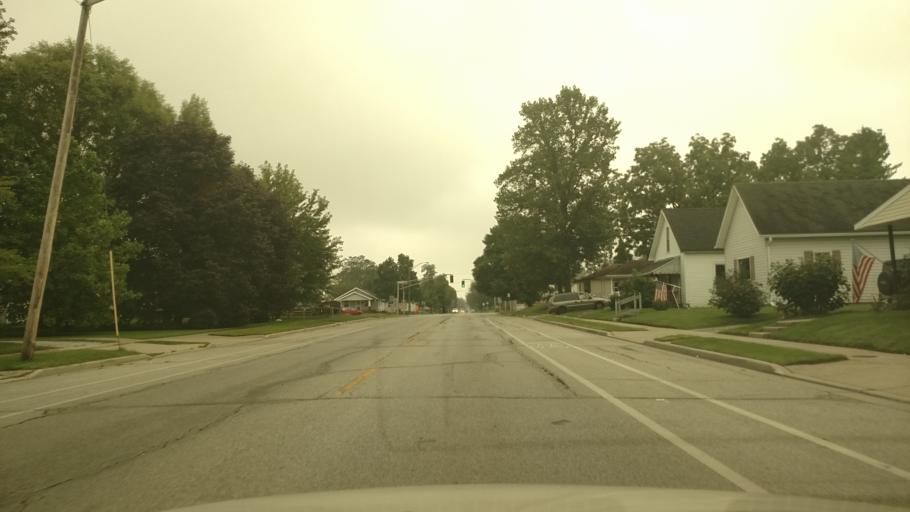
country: US
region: Indiana
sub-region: Howard County
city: Kokomo
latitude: 40.4995
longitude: -86.1270
